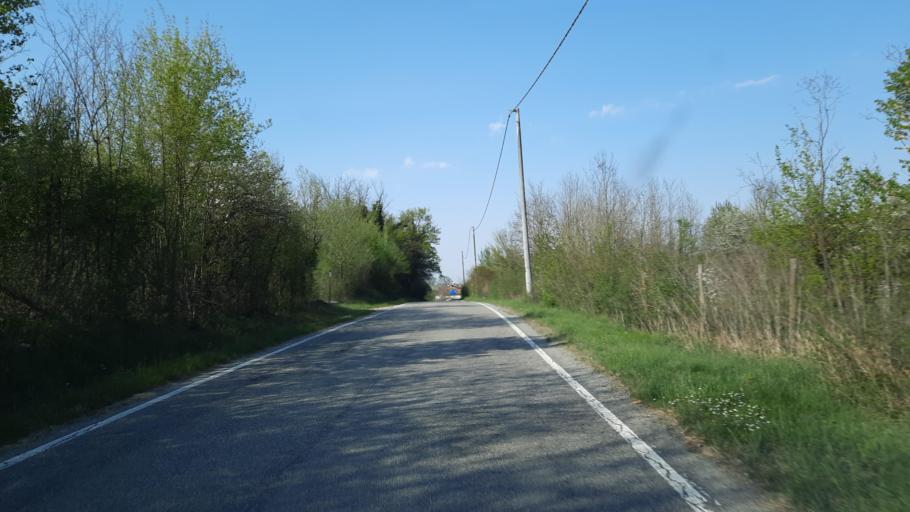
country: IT
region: Piedmont
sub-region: Provincia di Alessandria
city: Moncestino
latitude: 45.1545
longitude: 8.1759
